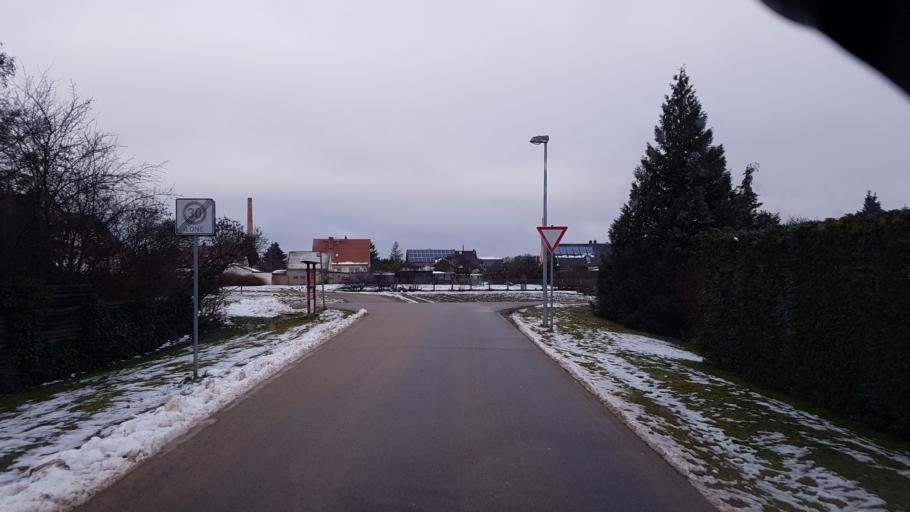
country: DE
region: Brandenburg
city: Luebben
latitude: 51.9407
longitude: 13.9177
